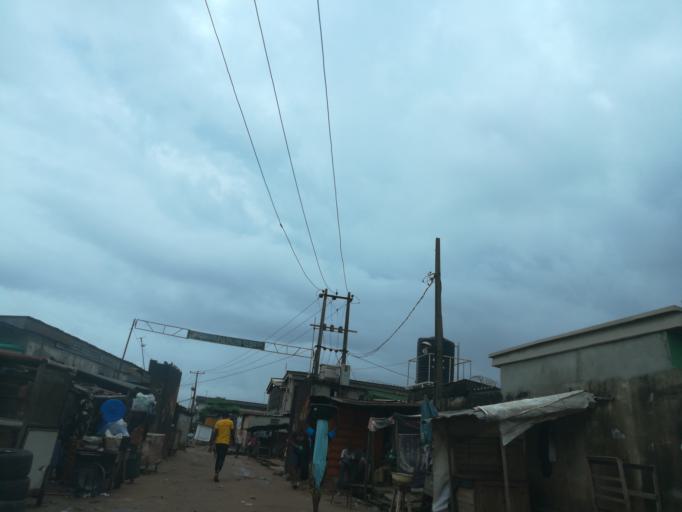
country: NG
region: Lagos
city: Agege
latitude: 6.6092
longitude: 3.3267
